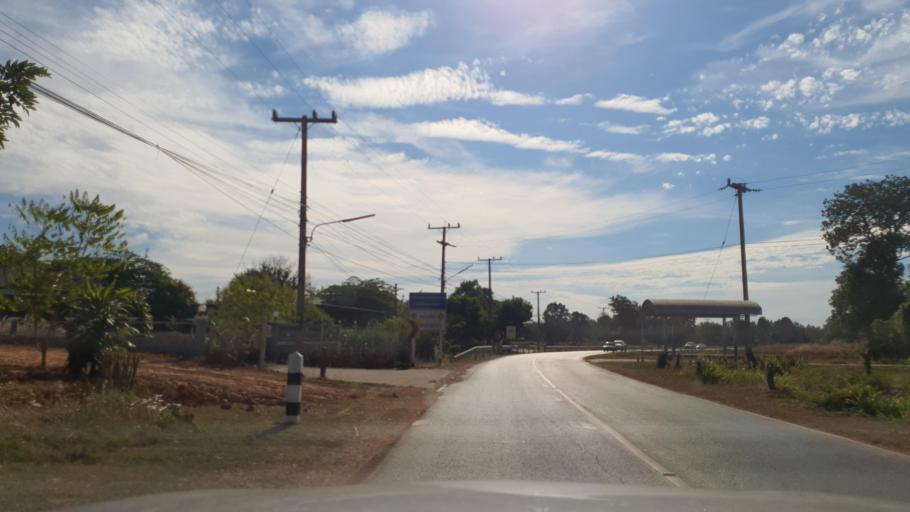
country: TH
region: Kalasin
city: Kuchinarai
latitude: 16.5439
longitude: 104.0930
